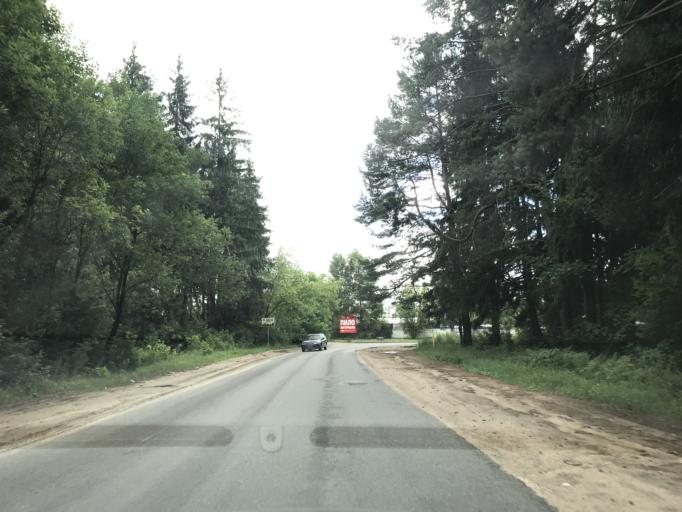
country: BY
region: Minsk
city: Borovlyany
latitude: 53.9595
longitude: 27.6904
